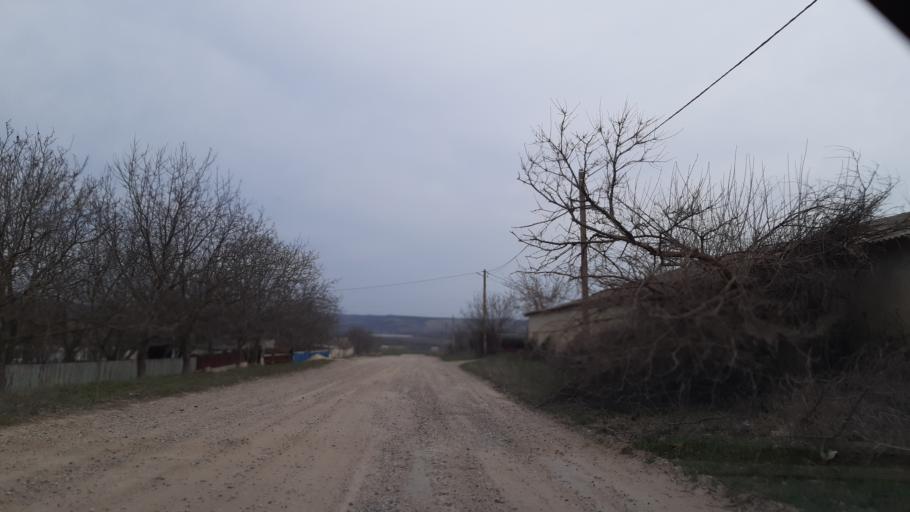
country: MD
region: Soldanesti
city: Soldanesti
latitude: 47.7098
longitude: 28.7084
